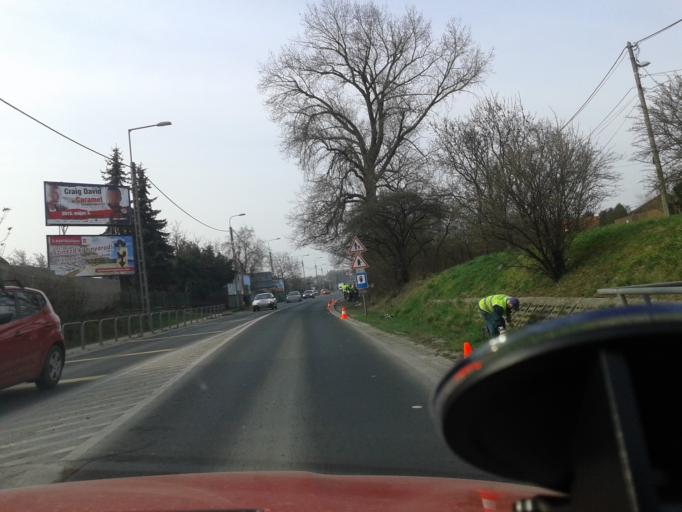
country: HU
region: Budapest
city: Budapest XXII. keruelet
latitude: 47.4318
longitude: 19.0047
